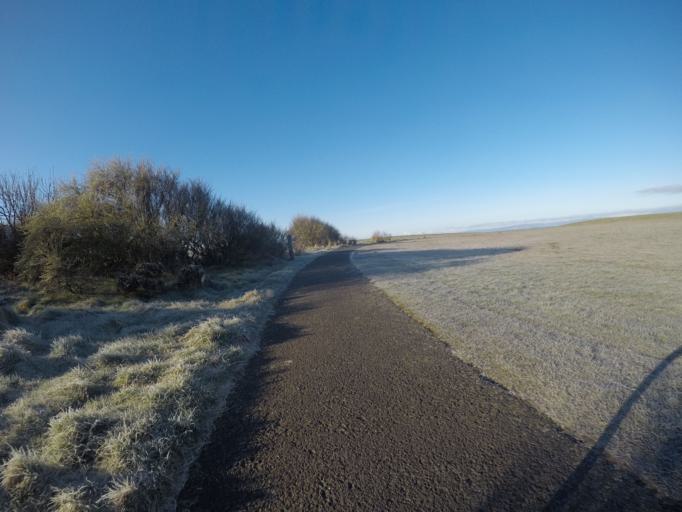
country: GB
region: Scotland
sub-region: North Ayrshire
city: Stevenston
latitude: 55.6263
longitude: -4.7457
